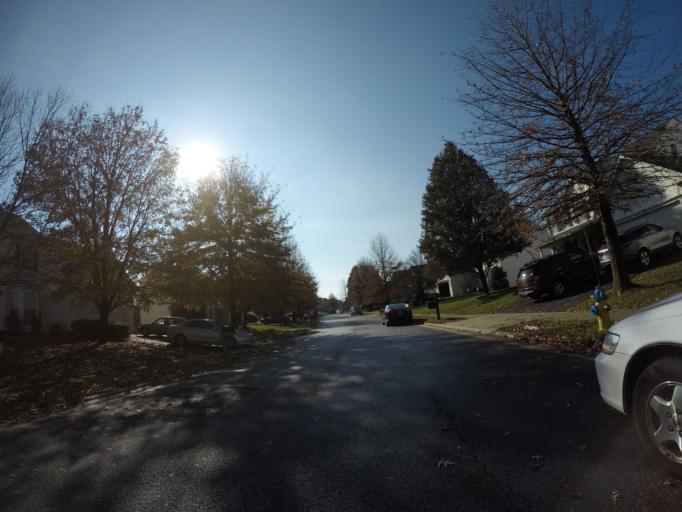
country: US
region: Maryland
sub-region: Frederick County
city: Ballenger Creek
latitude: 39.3723
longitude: -77.4383
